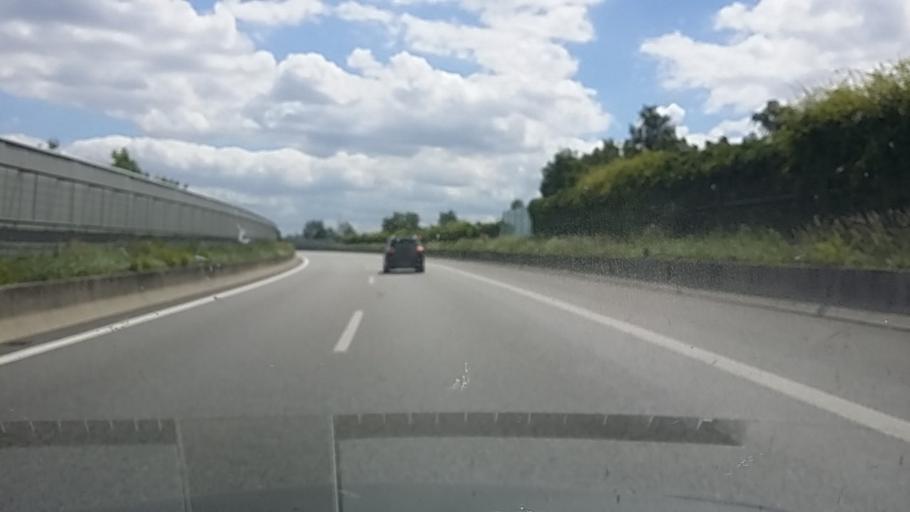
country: DE
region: Bavaria
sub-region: Upper Bavaria
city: Grobenzell
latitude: 48.2075
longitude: 11.3909
